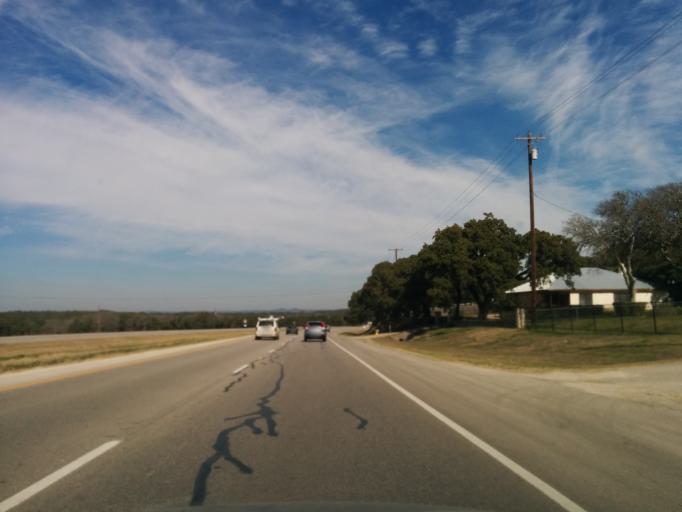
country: US
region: Texas
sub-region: Comal County
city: Bulverde
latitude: 29.8152
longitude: -98.4183
